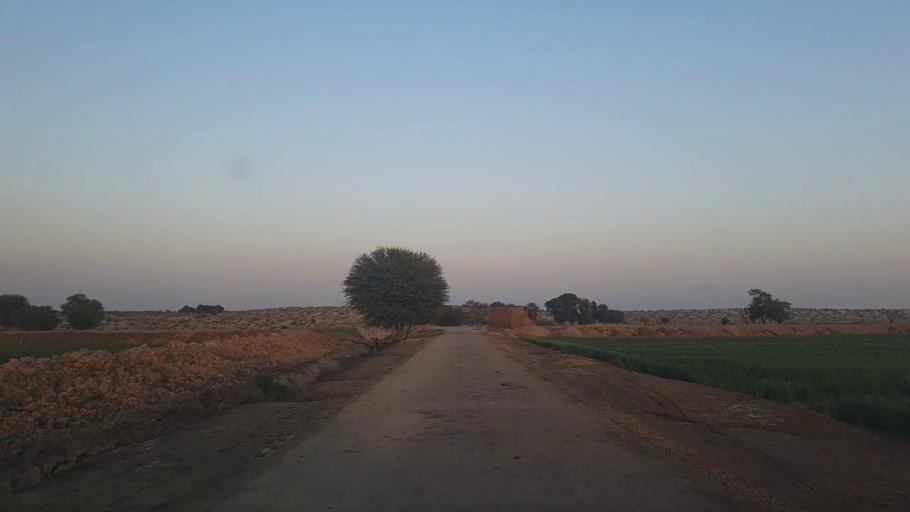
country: PK
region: Sindh
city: Jam Sahib
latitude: 26.3879
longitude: 68.7001
